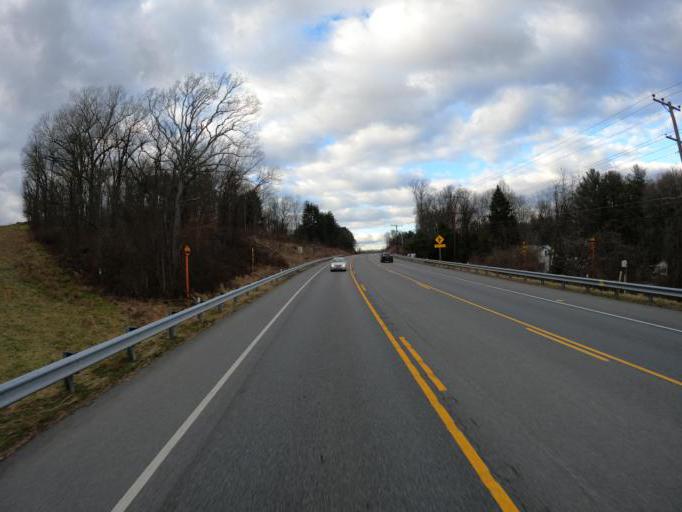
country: US
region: Maryland
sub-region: Carroll County
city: Sykesville
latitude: 39.3516
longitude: -76.9658
